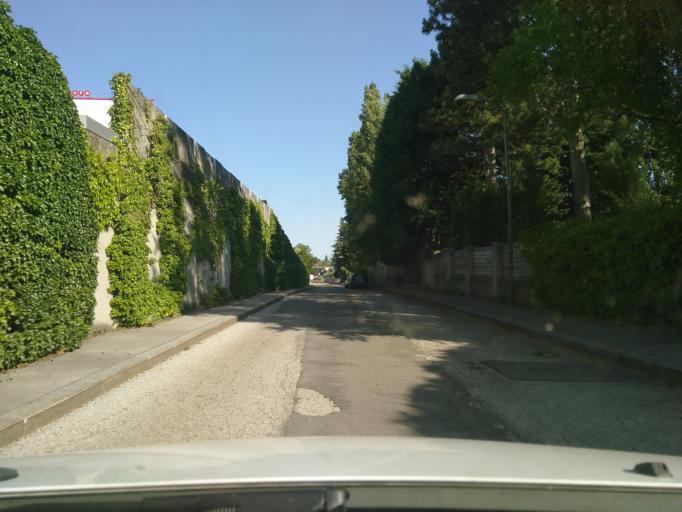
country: AT
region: Lower Austria
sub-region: Politischer Bezirk Modling
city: Perchtoldsdorf
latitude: 48.1768
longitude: 16.2899
